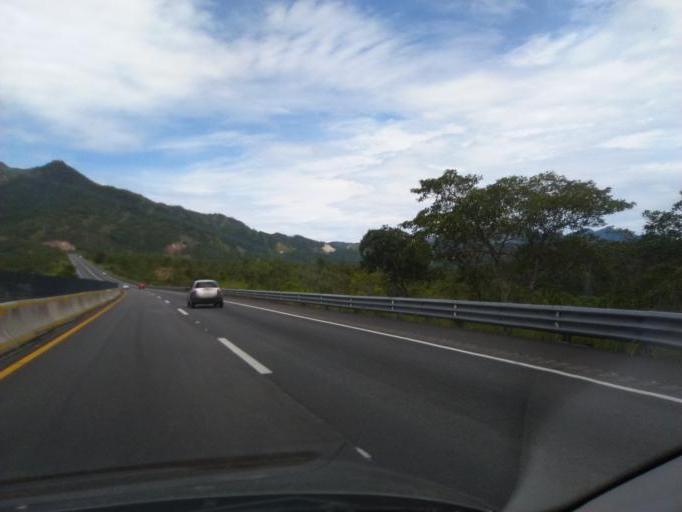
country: MX
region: Guerrero
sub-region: Chilpancingo de los Bravo
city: Cajelitos
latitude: 17.2849
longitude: -99.5060
